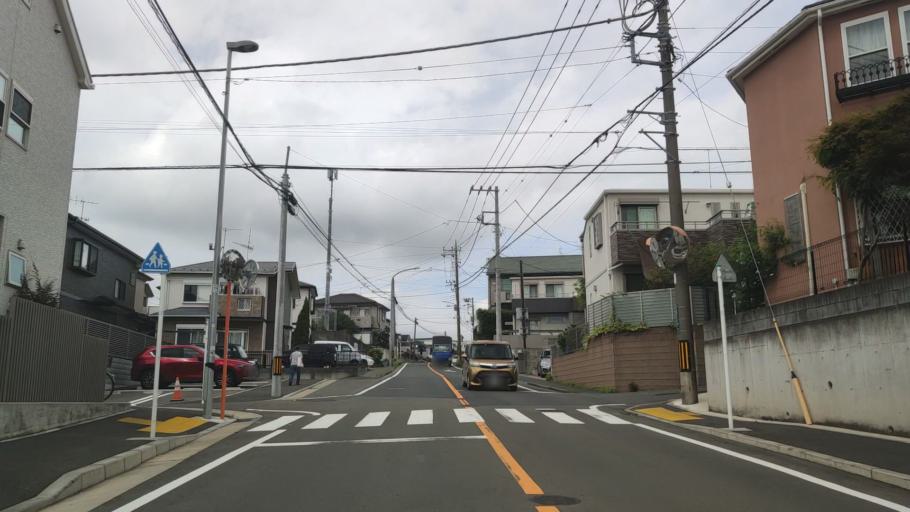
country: JP
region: Kanagawa
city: Minami-rinkan
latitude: 35.4758
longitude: 139.4760
